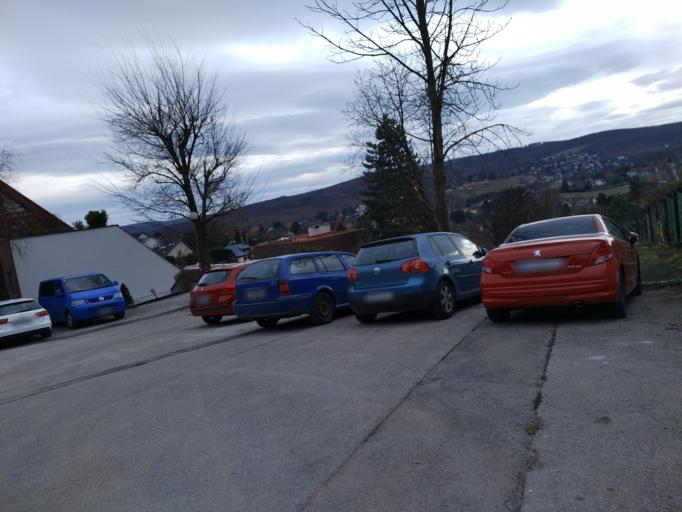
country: AT
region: Lower Austria
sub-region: Politischer Bezirk Wien-Umgebung
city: Gablitz
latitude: 48.2348
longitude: 16.1521
